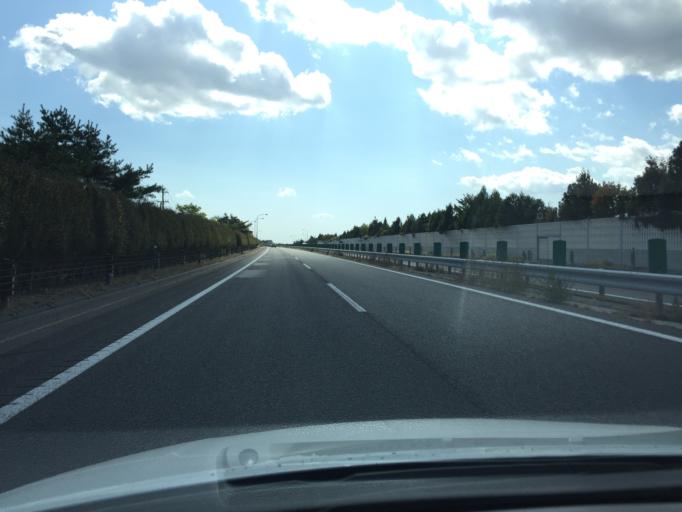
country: JP
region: Fukushima
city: Koriyama
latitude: 37.3916
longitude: 140.3111
